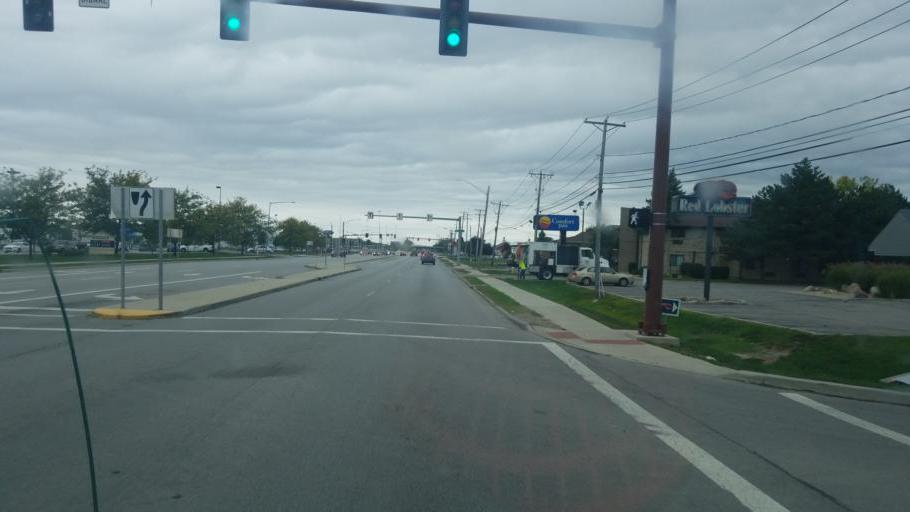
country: US
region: Ohio
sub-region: Lucas County
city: Maumee
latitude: 41.5832
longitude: -83.6648
